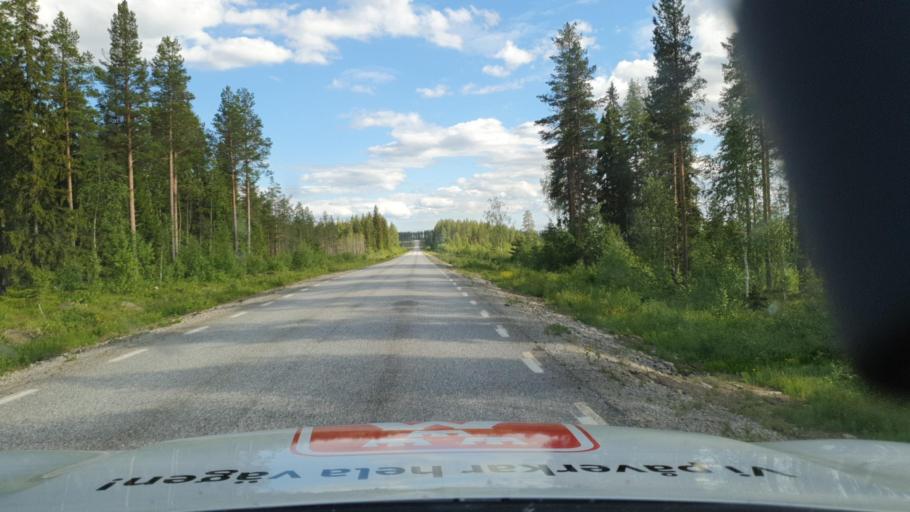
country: SE
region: Vaesterbotten
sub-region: Skelleftea Kommun
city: Langsele
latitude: 64.7135
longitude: 19.9821
